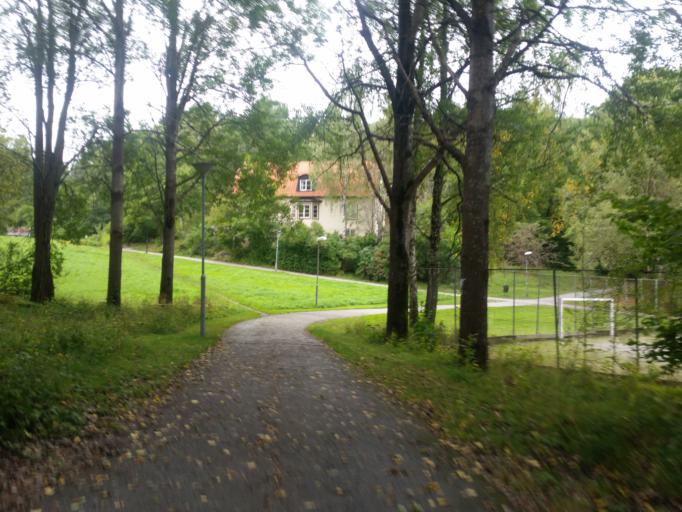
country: SE
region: Stockholm
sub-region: Stockholms Kommun
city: Arsta
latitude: 59.2536
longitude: 18.0951
